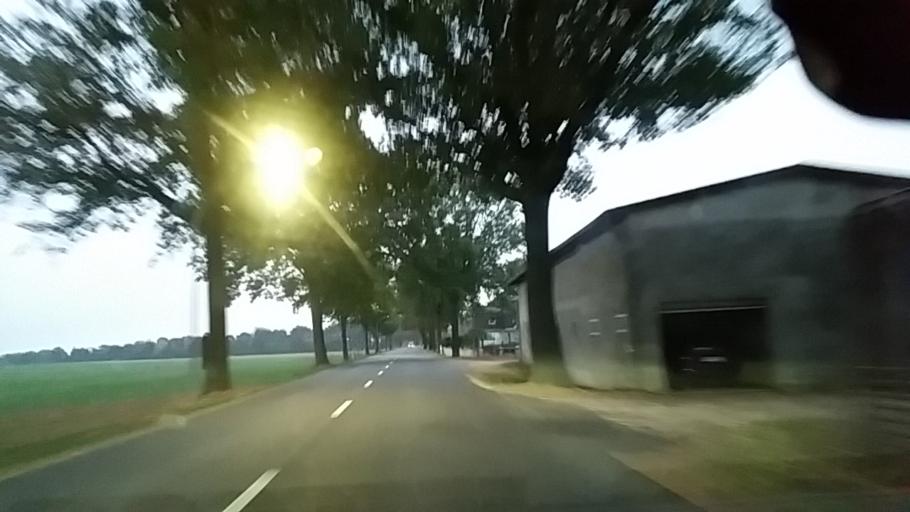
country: DE
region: Lower Saxony
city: Wittingen
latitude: 52.7239
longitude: 10.7506
